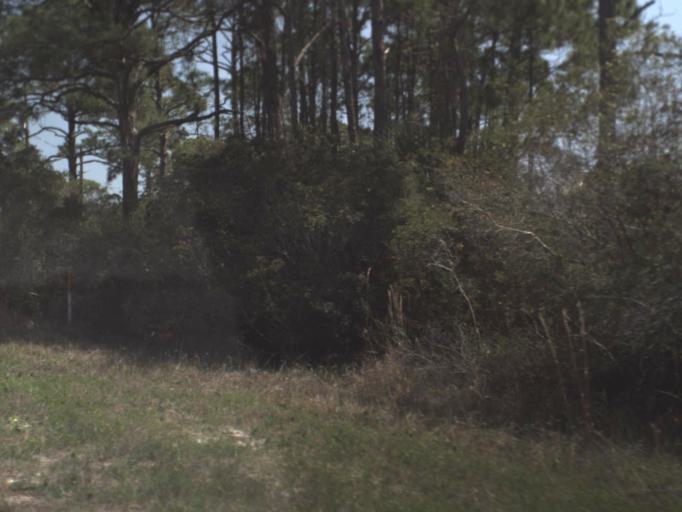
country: US
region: Florida
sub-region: Gulf County
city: Port Saint Joe
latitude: 29.6821
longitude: -85.3342
